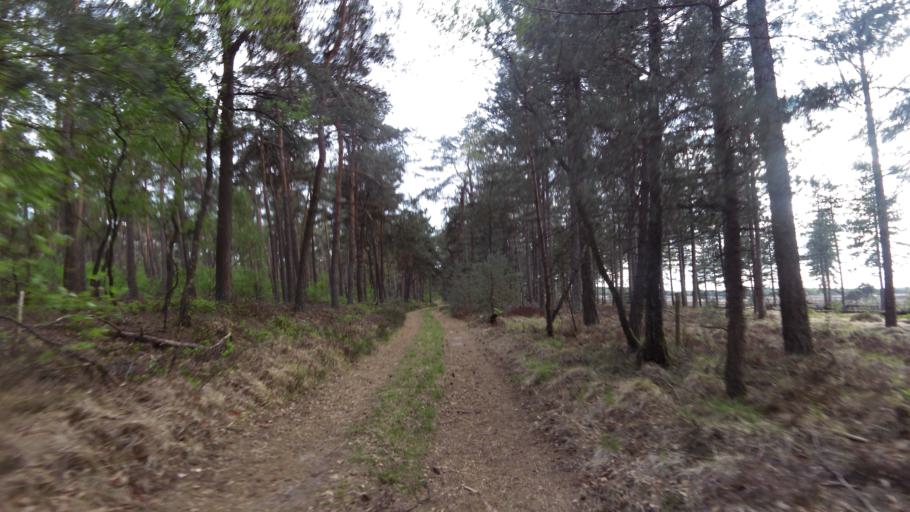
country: NL
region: Gelderland
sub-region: Gemeente Rozendaal
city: Rozendaal
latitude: 52.0355
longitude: 5.9539
